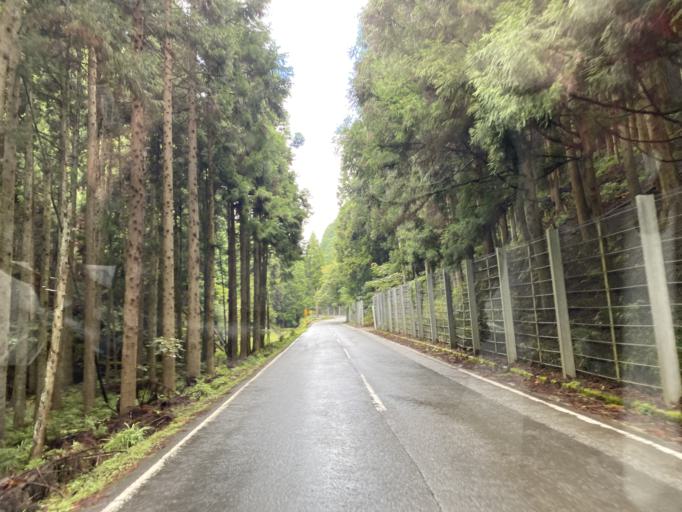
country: JP
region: Kyoto
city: Fukuchiyama
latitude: 35.2996
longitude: 134.9523
